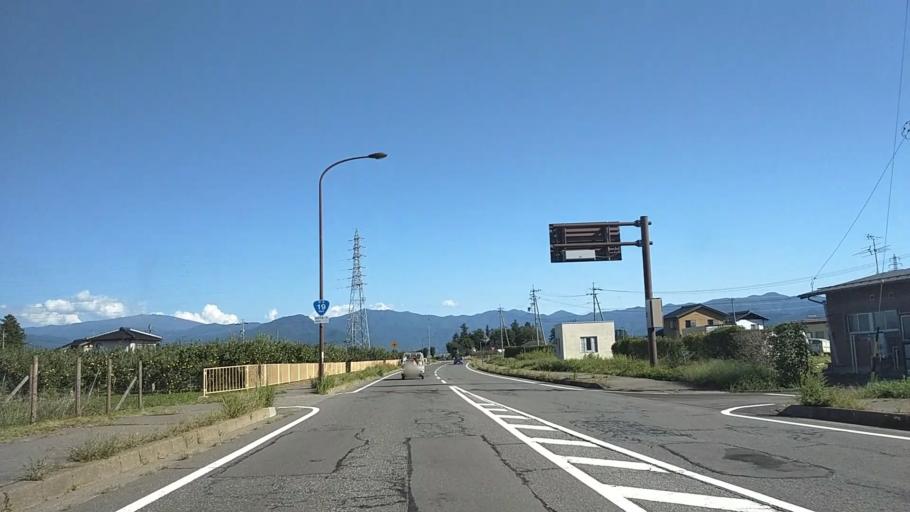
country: JP
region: Nagano
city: Nagano-shi
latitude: 36.6156
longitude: 138.1369
